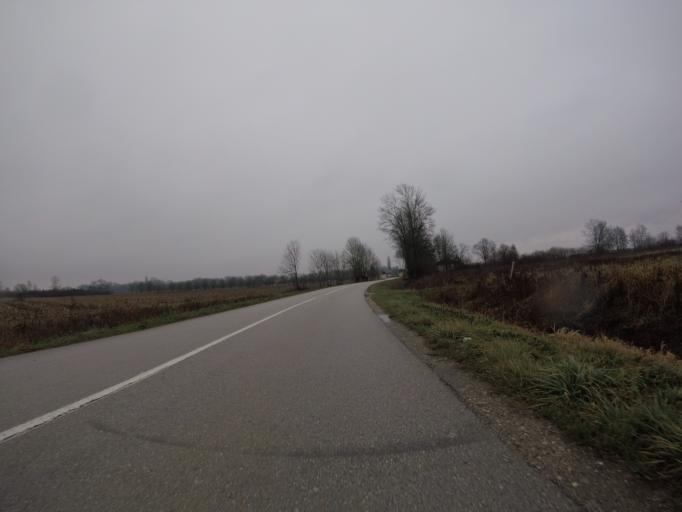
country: HR
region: Zagrebacka
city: Kuce
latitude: 45.7024
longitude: 16.2025
